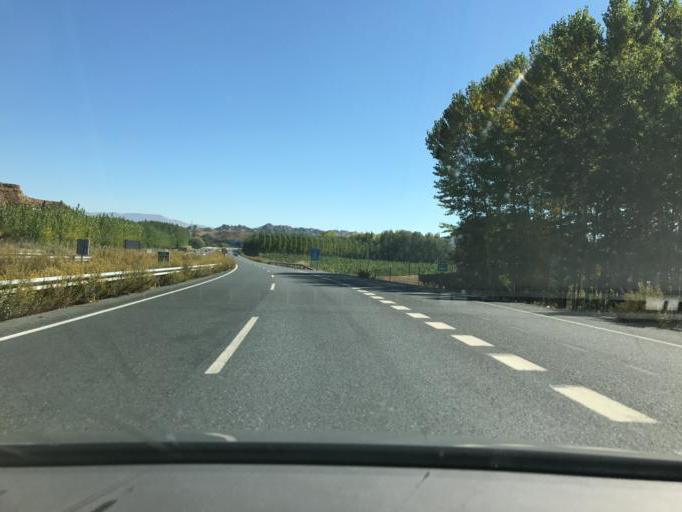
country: ES
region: Andalusia
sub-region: Provincia de Granada
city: Purullena
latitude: 37.3290
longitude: -3.2159
